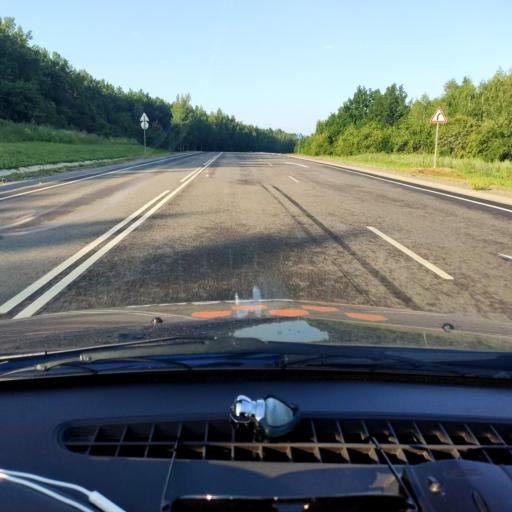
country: RU
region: Lipetsk
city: Izmalkovo
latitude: 52.4590
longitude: 38.0104
